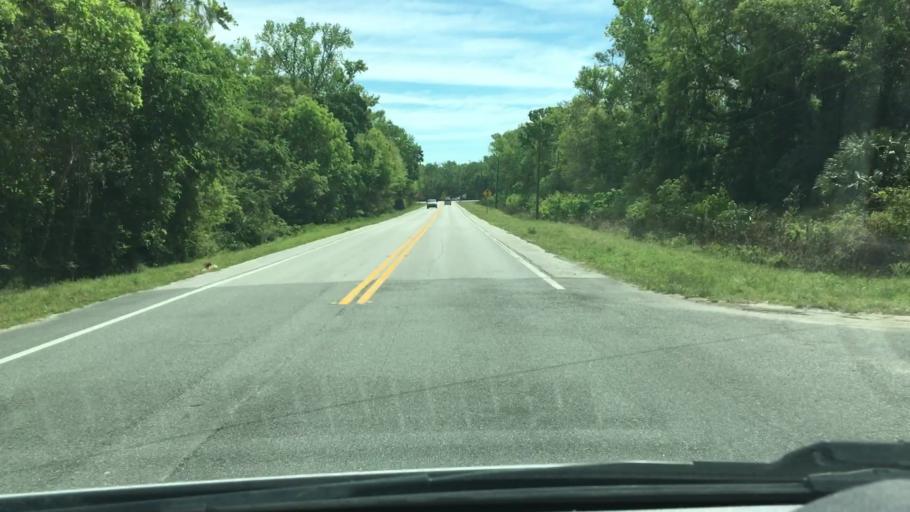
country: US
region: Florida
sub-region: Lake County
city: Lake Mack-Forest Hills
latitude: 29.0076
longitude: -81.3892
